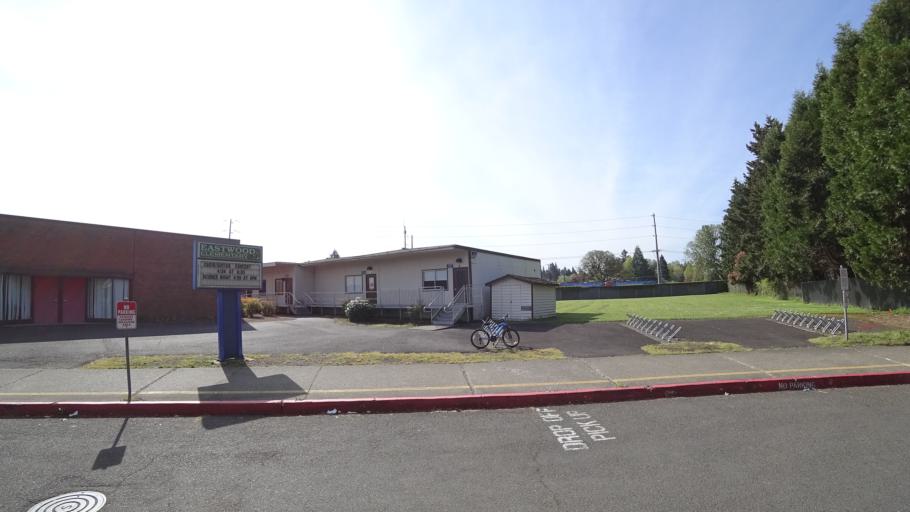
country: US
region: Oregon
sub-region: Washington County
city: Hillsboro
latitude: 45.5234
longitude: -122.9606
